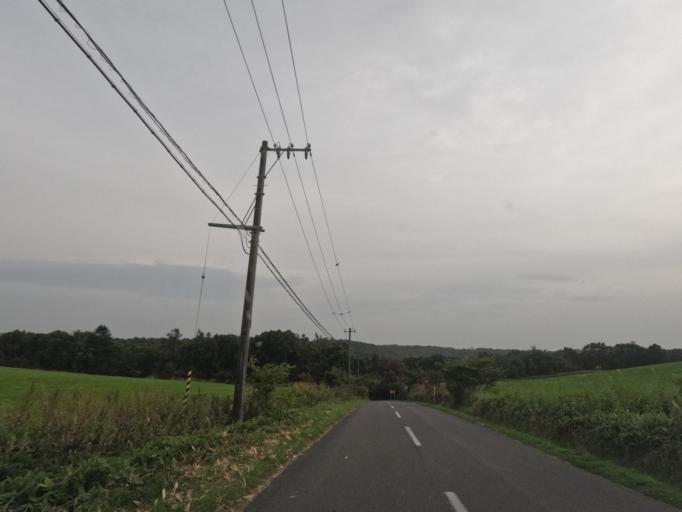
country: JP
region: Hokkaido
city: Date
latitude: 42.4044
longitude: 140.9246
